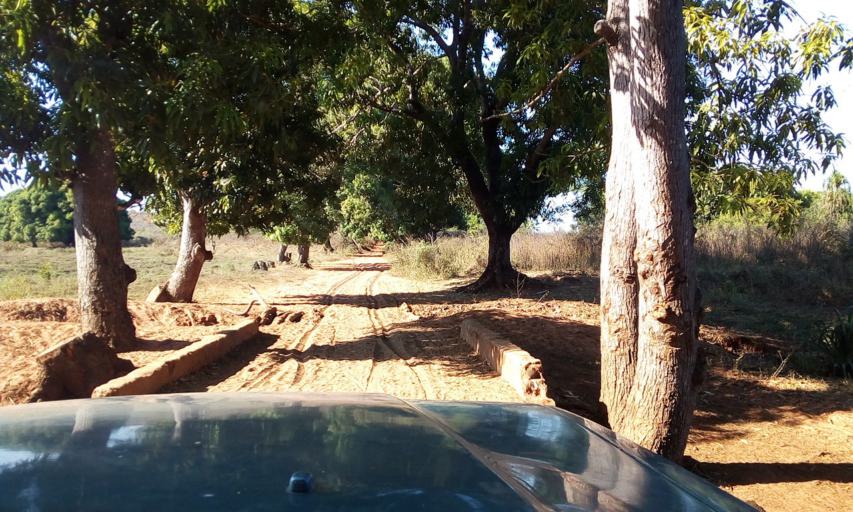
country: MG
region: Boeny
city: Sitampiky
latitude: -16.2207
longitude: 45.3652
